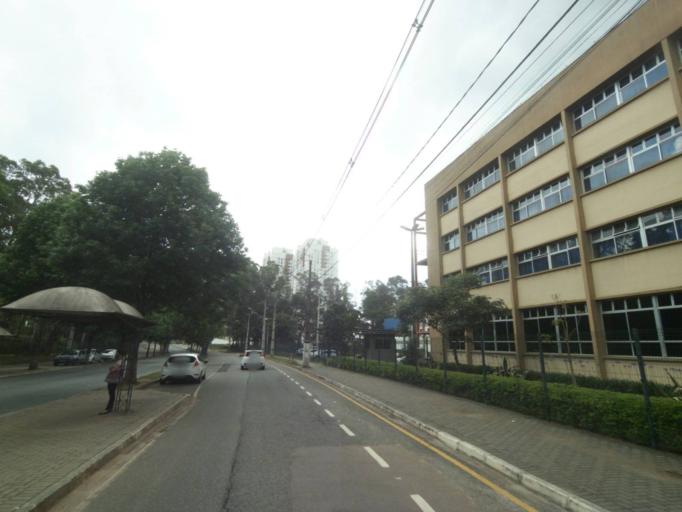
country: BR
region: Parana
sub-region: Curitiba
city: Curitiba
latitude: -25.4436
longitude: -49.3533
